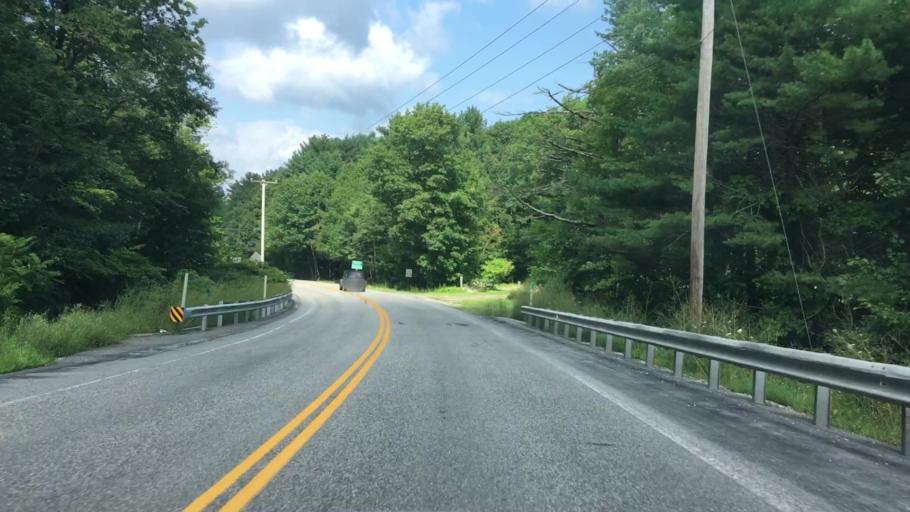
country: US
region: Maine
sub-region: Androscoggin County
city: Minot
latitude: 44.0282
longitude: -70.3015
